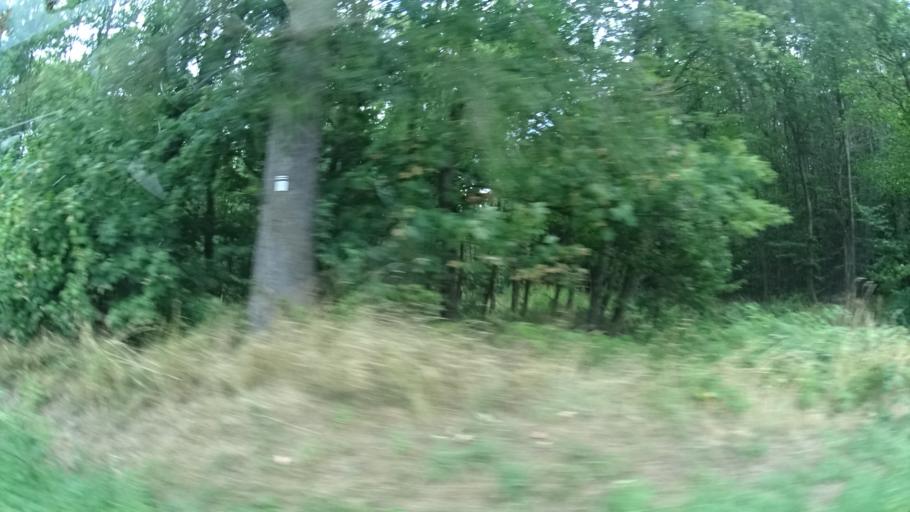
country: DE
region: Hesse
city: Gedern
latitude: 50.4016
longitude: 9.1959
